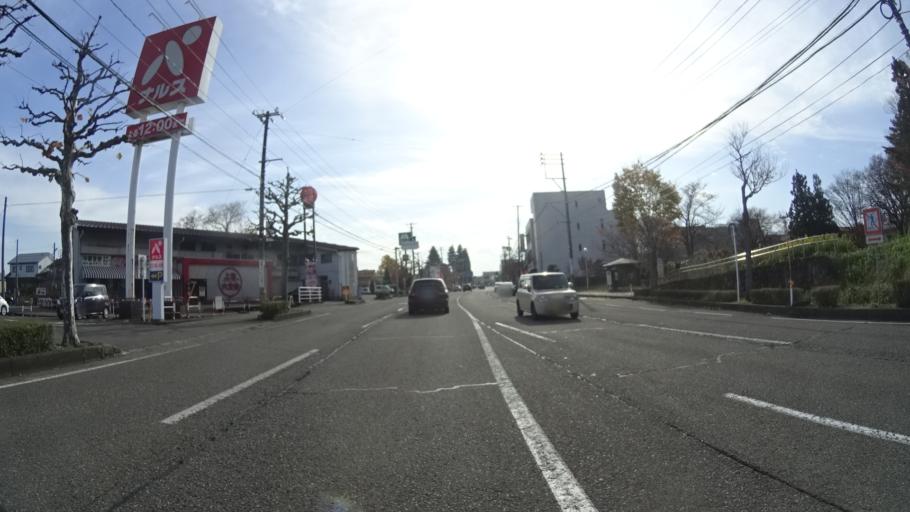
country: JP
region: Niigata
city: Joetsu
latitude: 37.1168
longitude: 138.2519
